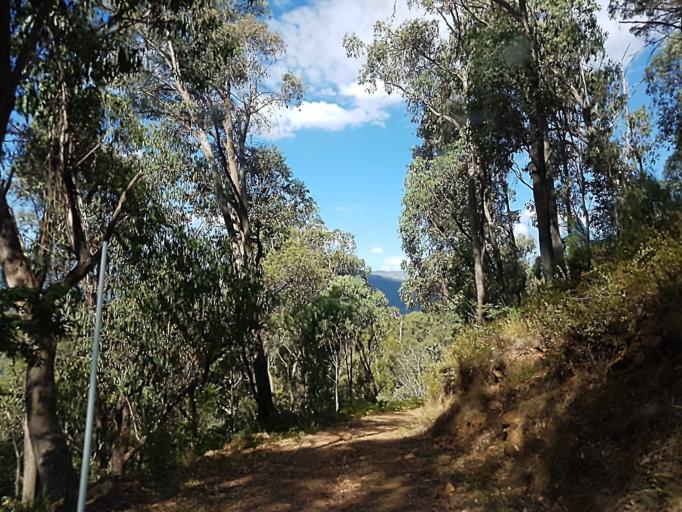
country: AU
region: Victoria
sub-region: Alpine
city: Mount Beauty
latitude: -36.9336
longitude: 146.9981
